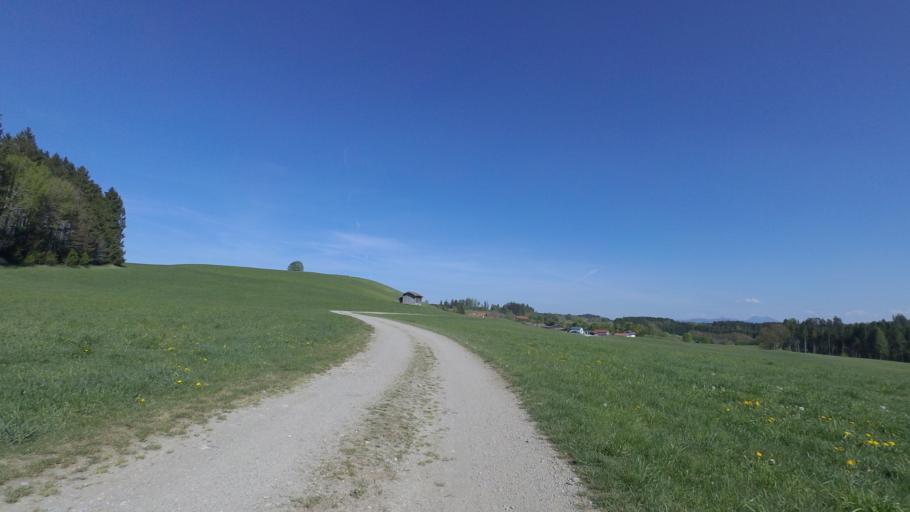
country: DE
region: Bavaria
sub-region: Upper Bavaria
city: Chieming
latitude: 47.9449
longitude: 12.5388
